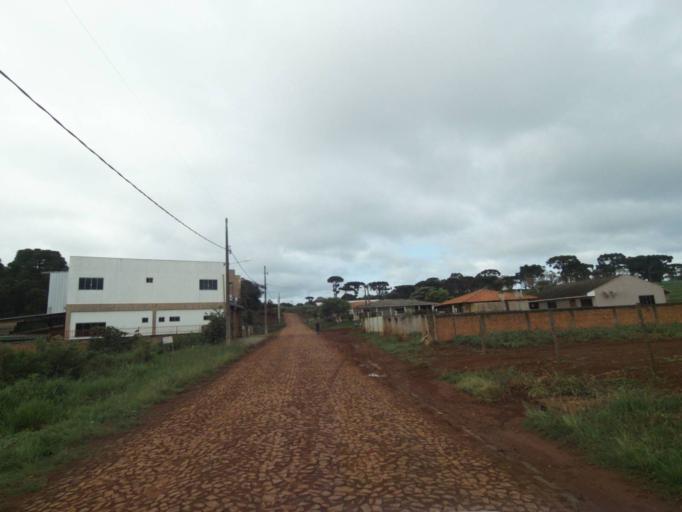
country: BR
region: Parana
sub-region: Pitanga
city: Pitanga
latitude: -24.9418
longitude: -51.8730
